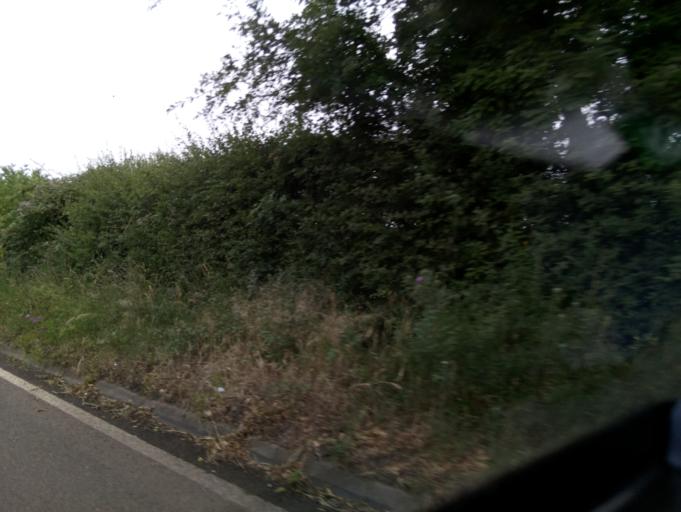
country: GB
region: England
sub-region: Gloucestershire
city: Tewkesbury
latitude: 52.0205
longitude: -2.1647
